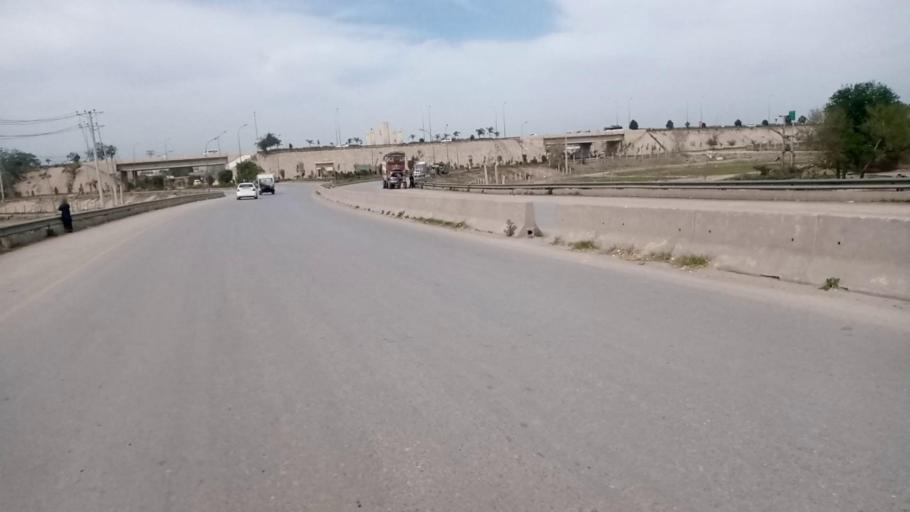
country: PK
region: Khyber Pakhtunkhwa
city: Peshawar
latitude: 34.0241
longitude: 71.6445
